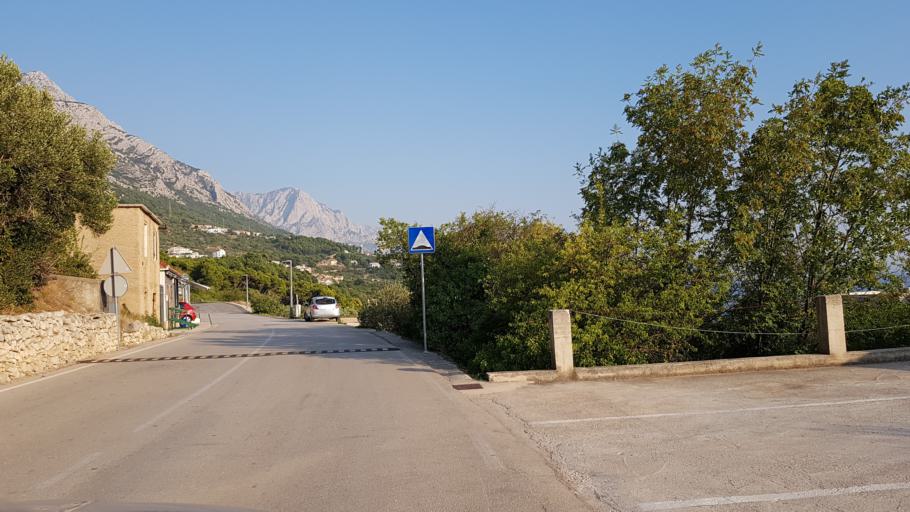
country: HR
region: Splitsko-Dalmatinska
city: Donja Brela
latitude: 43.3832
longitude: 16.9111
